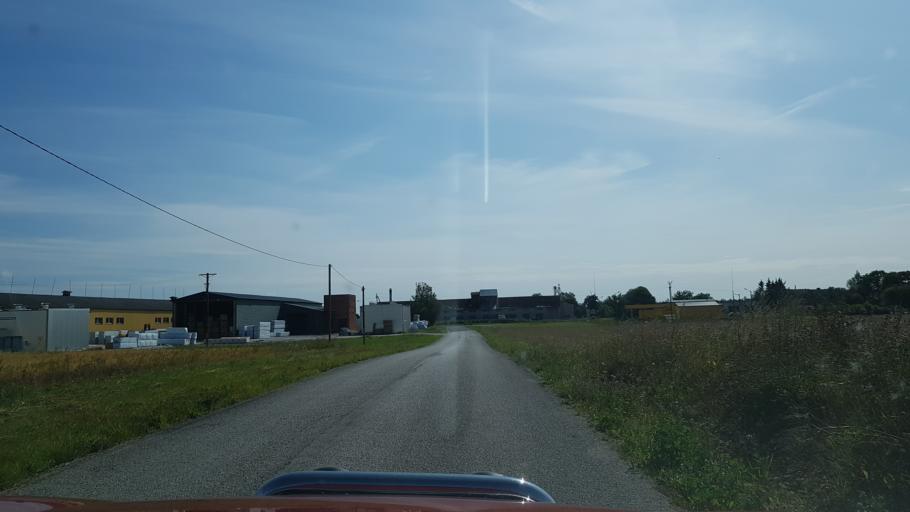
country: EE
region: Jaervamaa
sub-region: Jaerva-Jaani vald
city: Jarva-Jaani
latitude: 59.1176
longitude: 25.7239
